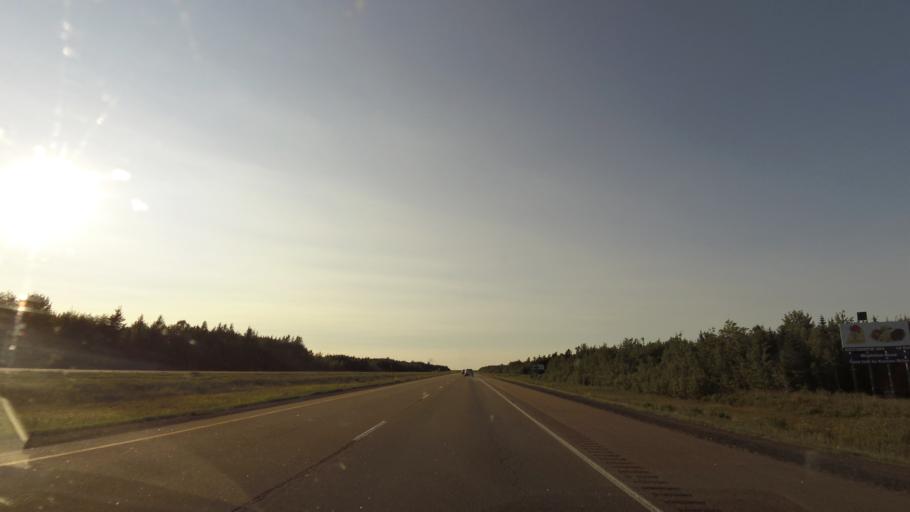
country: CA
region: New Brunswick
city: Dieppe
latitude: 46.1115
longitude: -64.6146
